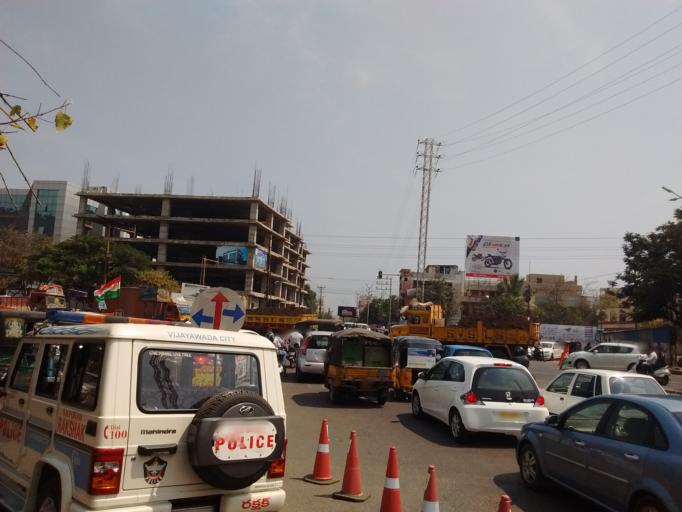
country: IN
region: Andhra Pradesh
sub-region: Krishna
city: Yanamalakuduru
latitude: 16.5052
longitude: 80.6611
